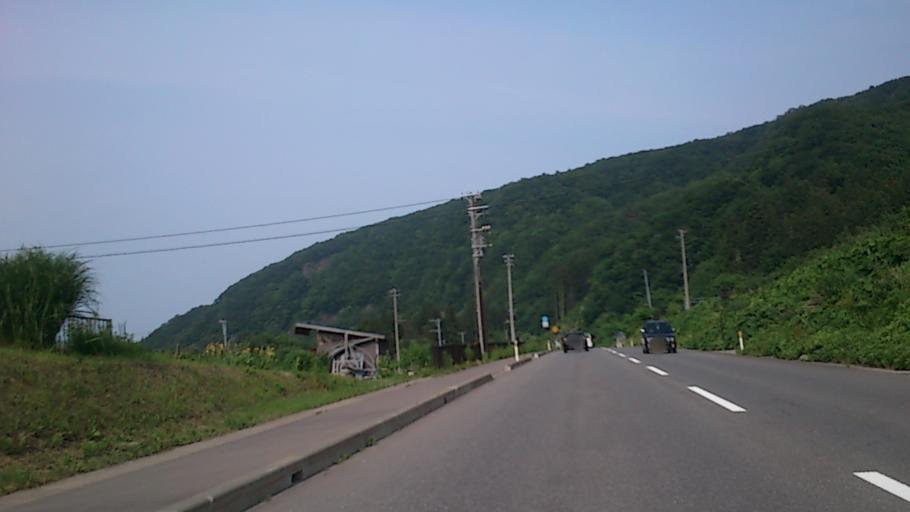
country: JP
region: Aomori
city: Hirosaki
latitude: 40.5642
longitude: 140.2862
